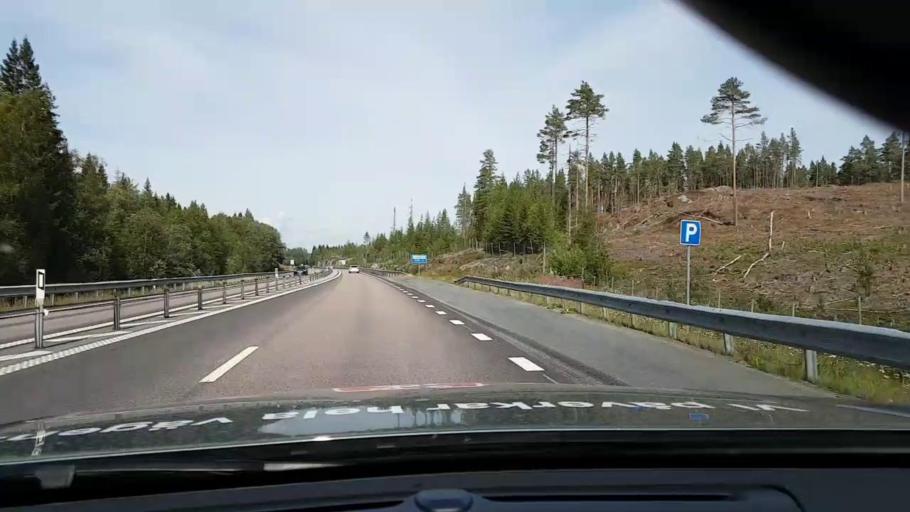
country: SE
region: Vaesternorrland
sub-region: OErnskoeldsviks Kommun
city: Husum
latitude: 63.4308
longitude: 19.2093
